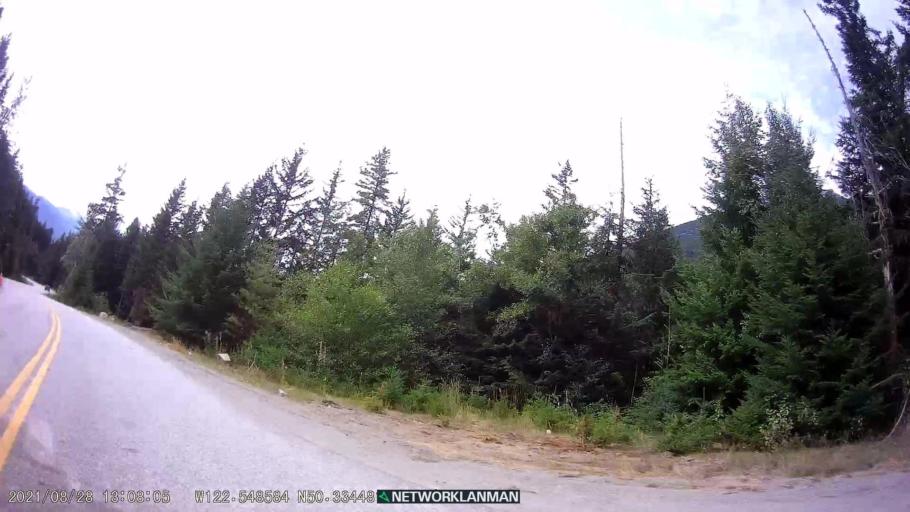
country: CA
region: British Columbia
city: Pemberton
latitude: 50.3344
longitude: -122.5490
